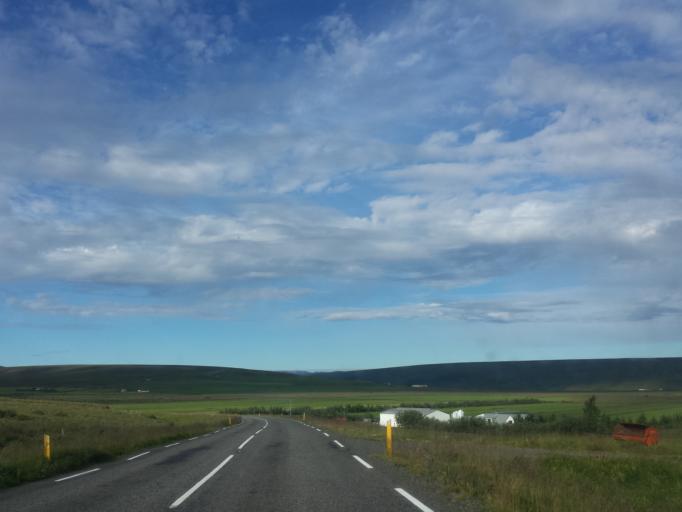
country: IS
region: Northeast
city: Laugar
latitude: 65.7118
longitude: -17.6081
